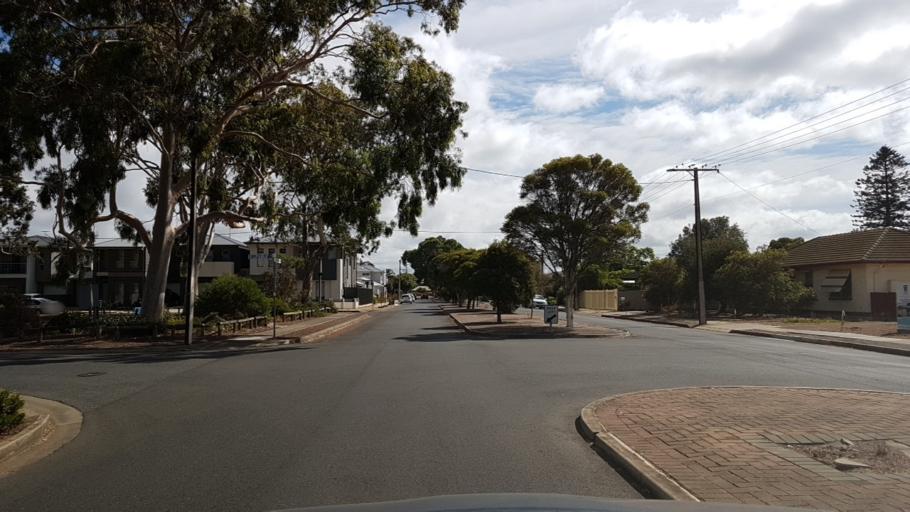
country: AU
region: South Australia
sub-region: Marion
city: Plympton Park
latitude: -34.9935
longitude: 138.5513
